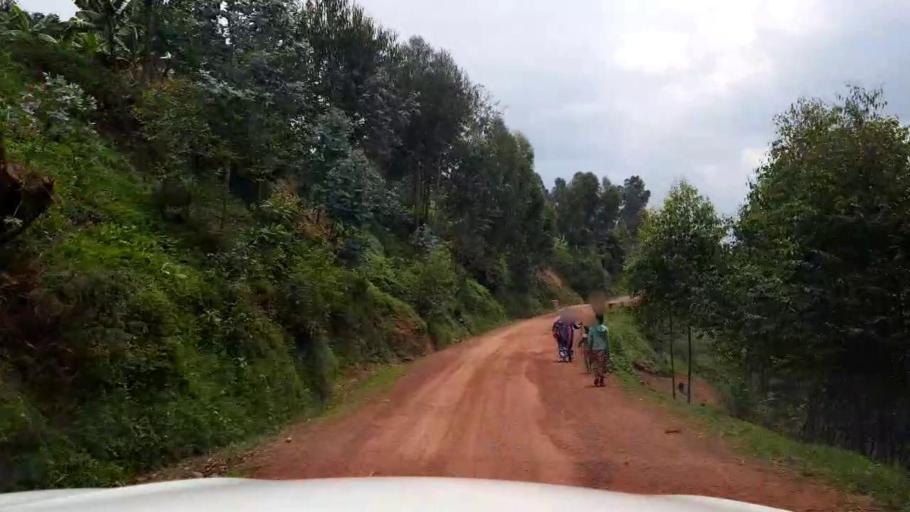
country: RW
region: Northern Province
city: Byumba
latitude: -1.4961
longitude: 29.9347
